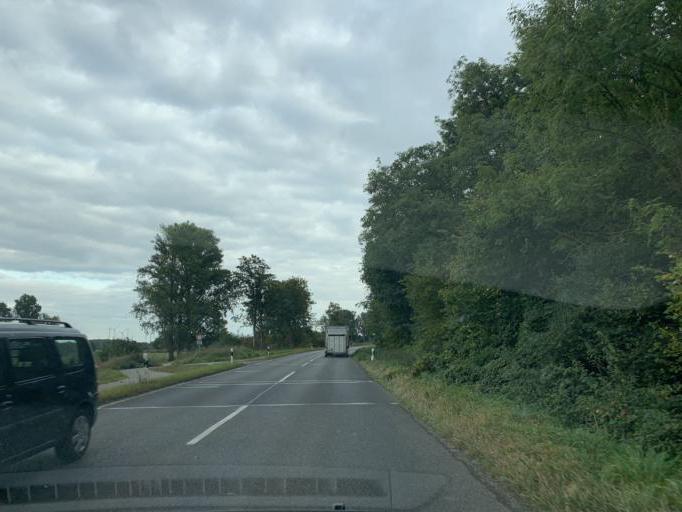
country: DE
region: North Rhine-Westphalia
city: Huckelhoven
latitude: 51.0258
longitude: 6.2245
